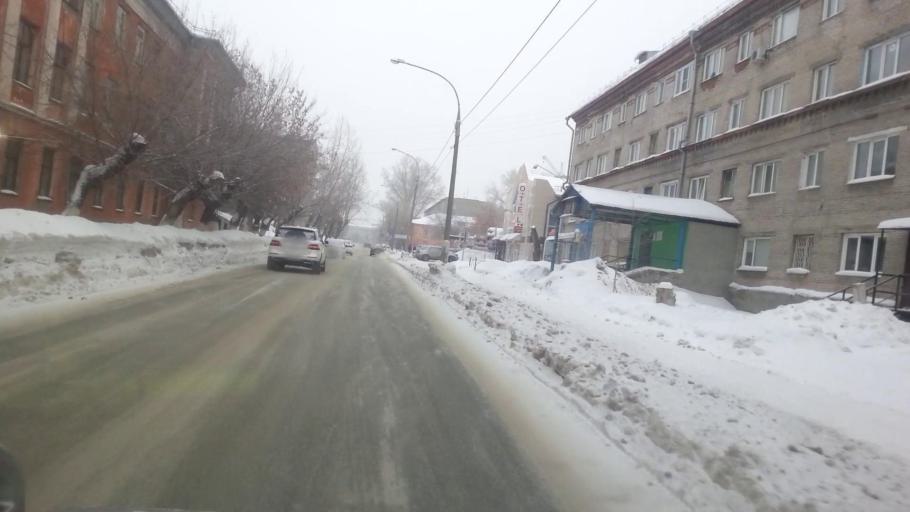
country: RU
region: Altai Krai
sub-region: Gorod Barnaulskiy
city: Barnaul
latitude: 53.3807
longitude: 83.7329
